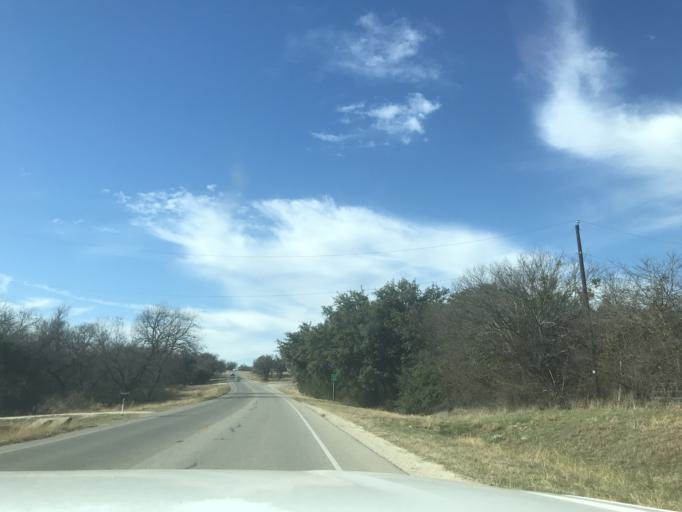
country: US
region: Texas
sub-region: Erath County
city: Stephenville
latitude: 32.2053
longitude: -98.1879
